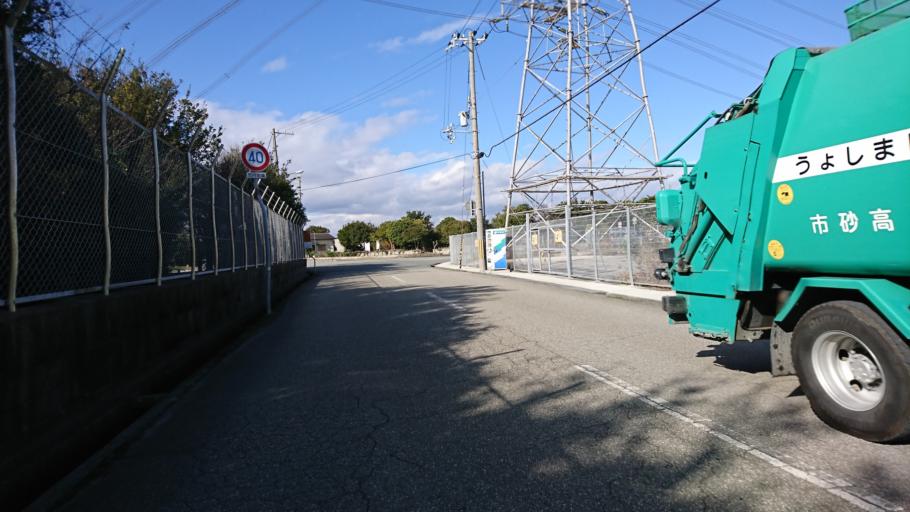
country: JP
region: Hyogo
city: Shirahamacho-usazakiminami
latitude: 34.7573
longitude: 134.7657
